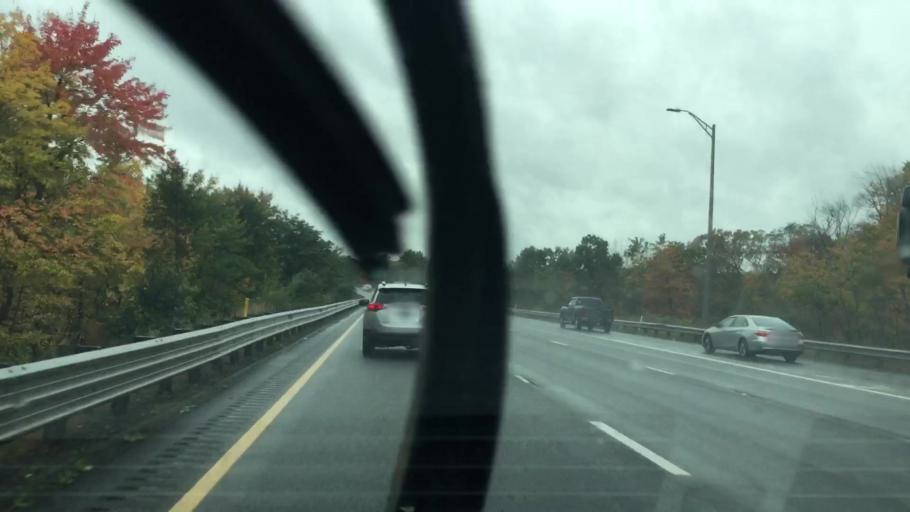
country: US
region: Massachusetts
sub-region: Essex County
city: Haverhill
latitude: 42.8004
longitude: -71.0936
